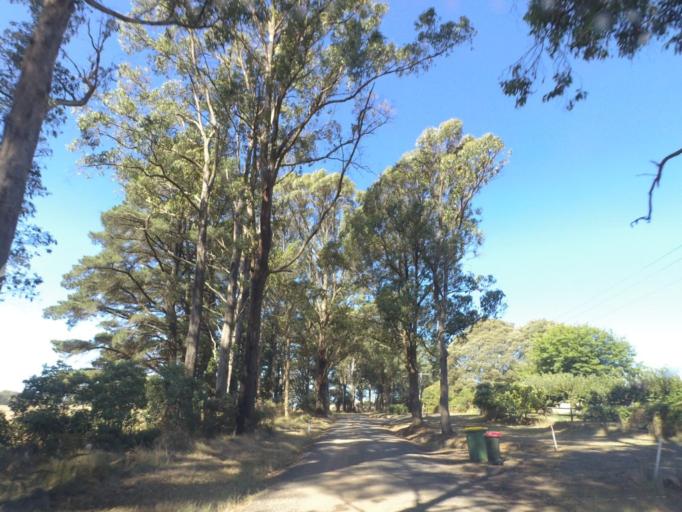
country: AU
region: Victoria
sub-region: Murrindindi
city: Kinglake West
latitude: -37.4759
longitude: 145.3271
